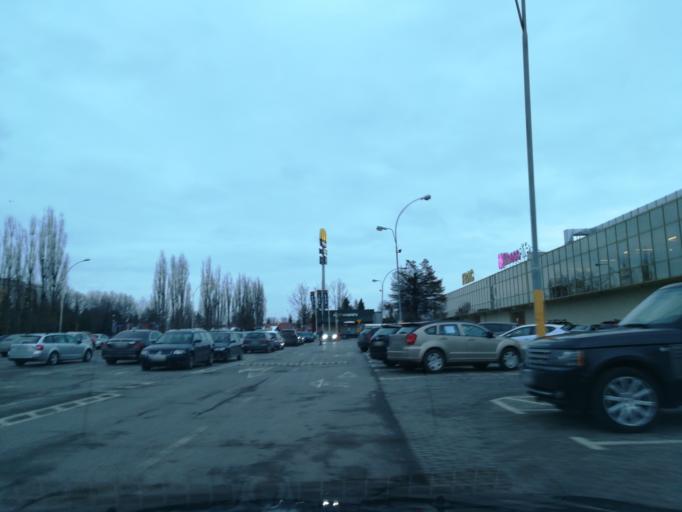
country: PL
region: Subcarpathian Voivodeship
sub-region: Rzeszow
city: Rzeszow
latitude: 50.0365
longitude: 22.0223
